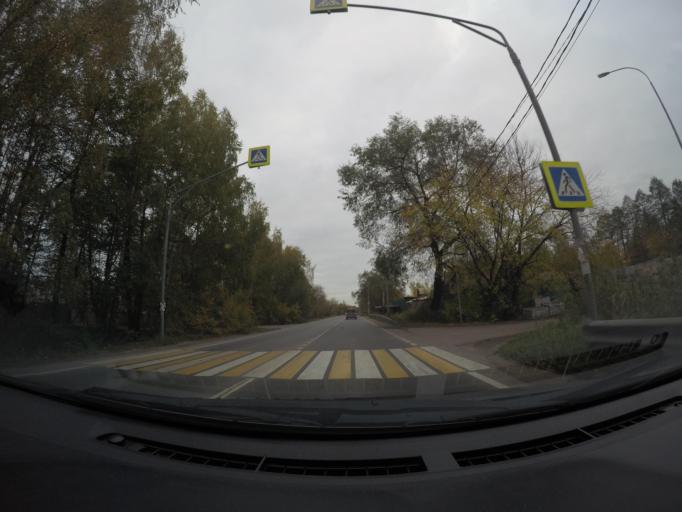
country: RU
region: Moskovskaya
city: Imeni Vorovskogo
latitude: 55.7224
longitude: 38.3481
